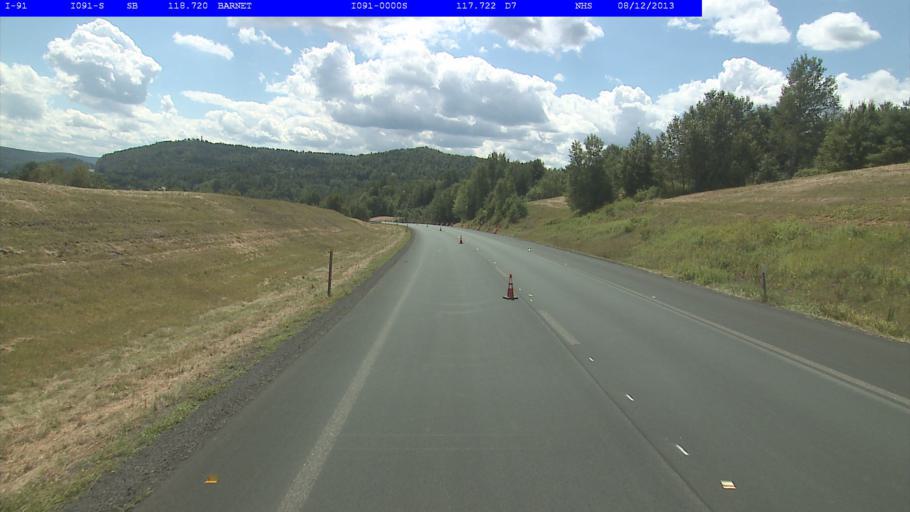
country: US
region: New Hampshire
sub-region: Grafton County
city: Woodsville
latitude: 44.2761
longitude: -72.0723
